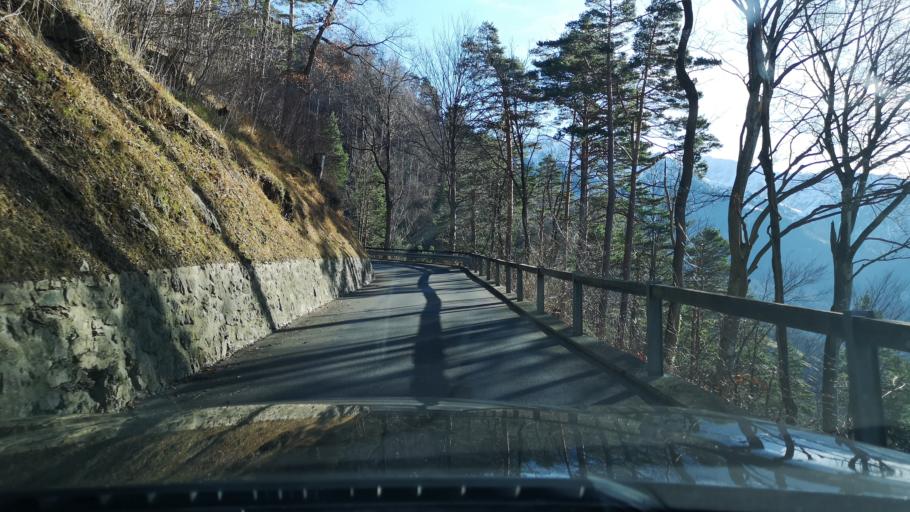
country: LI
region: Triesenberg
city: Triesenberg
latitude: 47.1242
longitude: 9.5342
